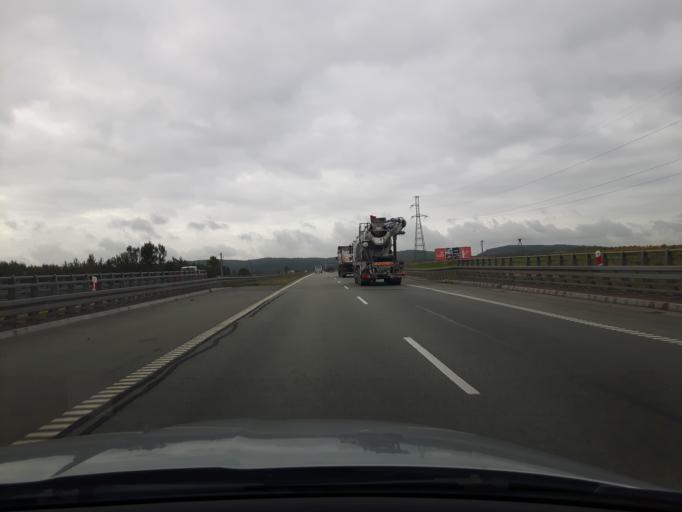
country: PL
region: Swietokrzyskie
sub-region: Powiat kielecki
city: Piekoszow
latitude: 50.8750
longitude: 20.5183
